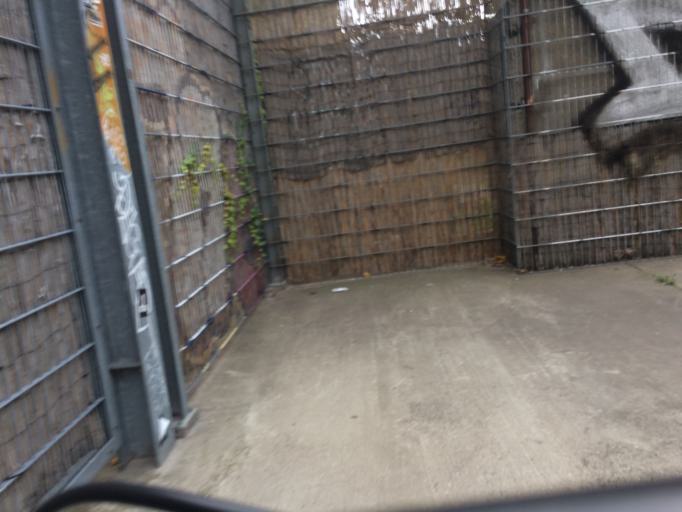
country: DE
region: Berlin
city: Friedrichshain Bezirk
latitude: 52.5109
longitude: 13.4432
